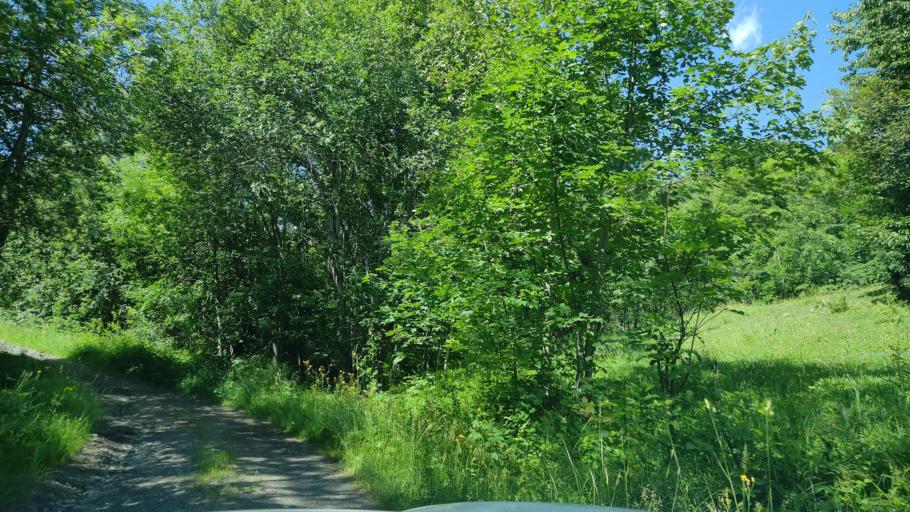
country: FR
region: Rhone-Alpes
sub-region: Departement de la Savoie
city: Saint-Jean-de-Maurienne
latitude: 45.2343
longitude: 6.2771
